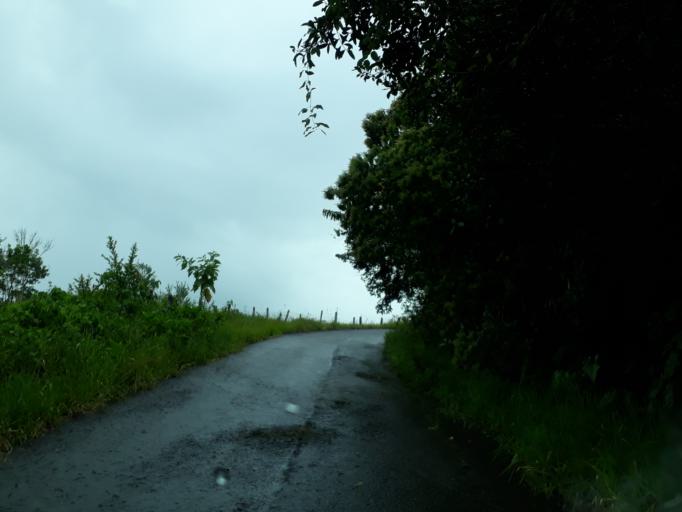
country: CO
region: Cundinamarca
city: Medina
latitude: 4.6838
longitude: -73.3133
